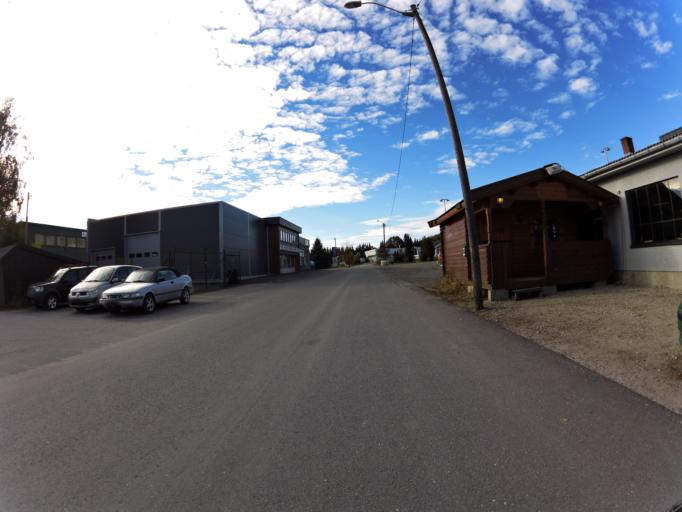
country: NO
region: Ostfold
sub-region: Sarpsborg
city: Sarpsborg
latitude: 59.2903
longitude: 11.0884
